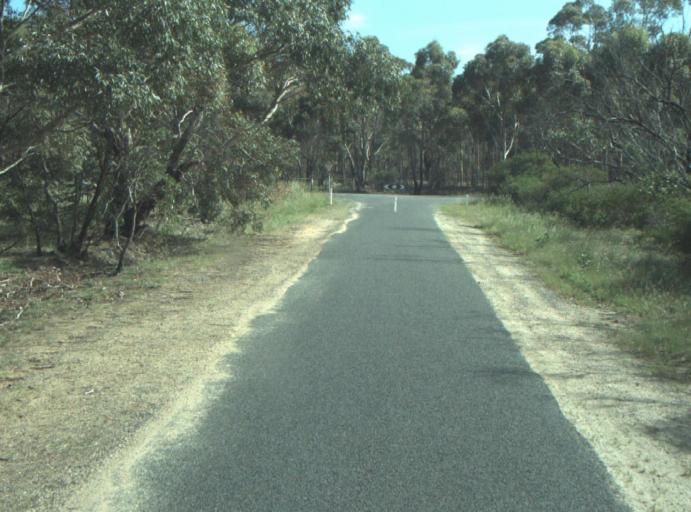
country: AU
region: Victoria
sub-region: Greater Geelong
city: Lara
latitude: -37.9682
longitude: 144.4249
